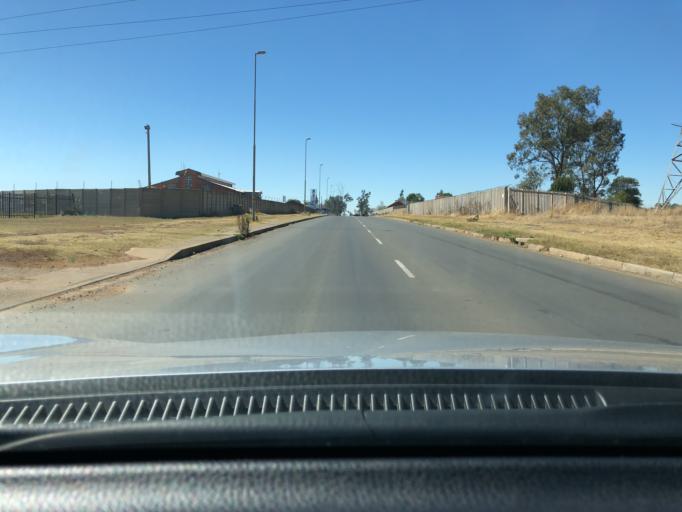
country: ZA
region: KwaZulu-Natal
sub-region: Amajuba District Municipality
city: Newcastle
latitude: -27.7604
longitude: 29.9481
